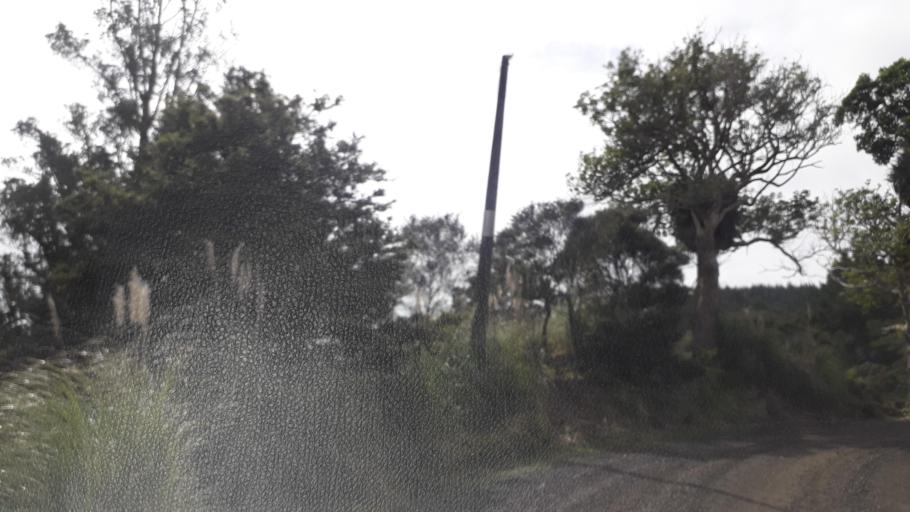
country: NZ
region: Northland
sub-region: Far North District
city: Kaitaia
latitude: -35.3756
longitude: 173.4111
